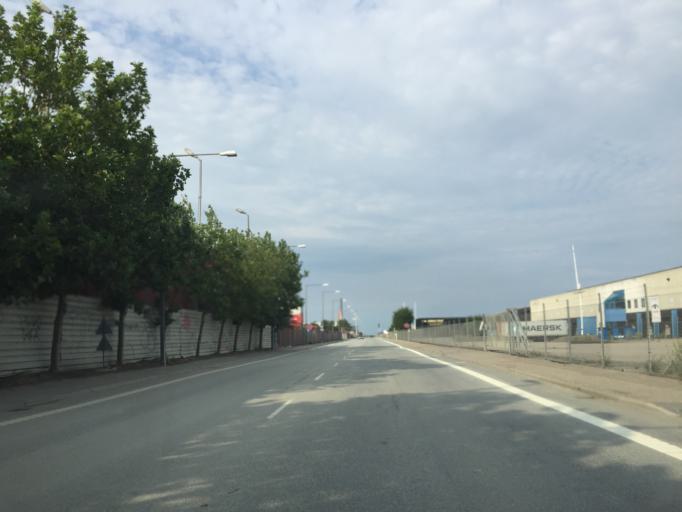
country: DK
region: Capital Region
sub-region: Gentofte Kommune
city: Charlottenlund
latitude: 55.7169
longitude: 12.6058
